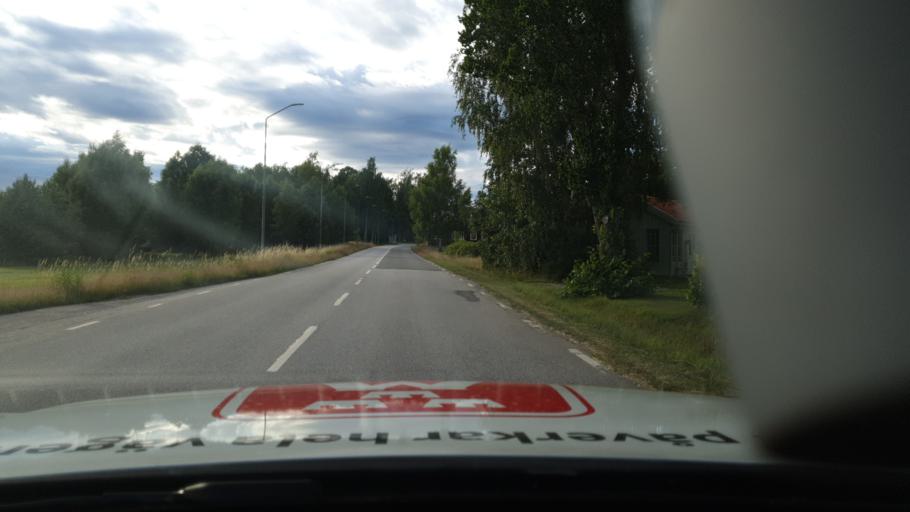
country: SE
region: Vaestra Goetaland
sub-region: Toreboda Kommun
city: Toereboda
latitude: 58.8317
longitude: 13.9835
